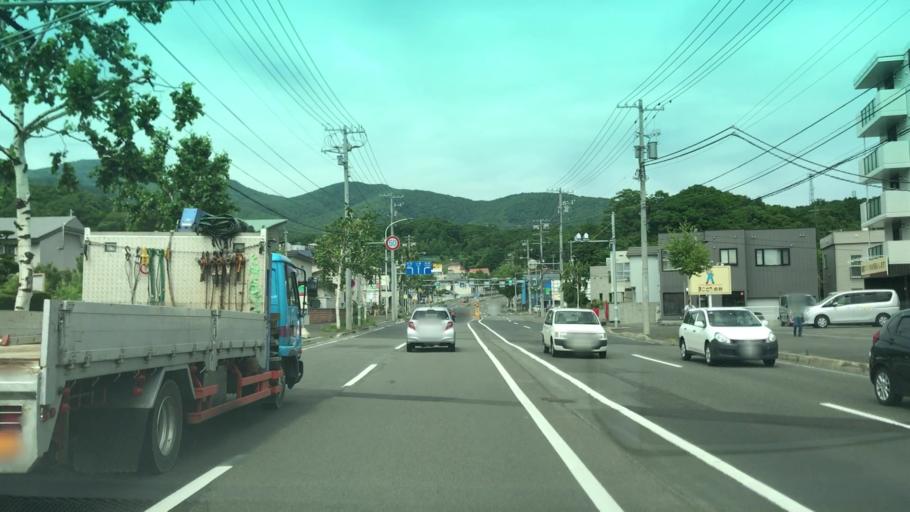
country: JP
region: Hokkaido
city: Sapporo
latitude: 43.0785
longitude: 141.2707
